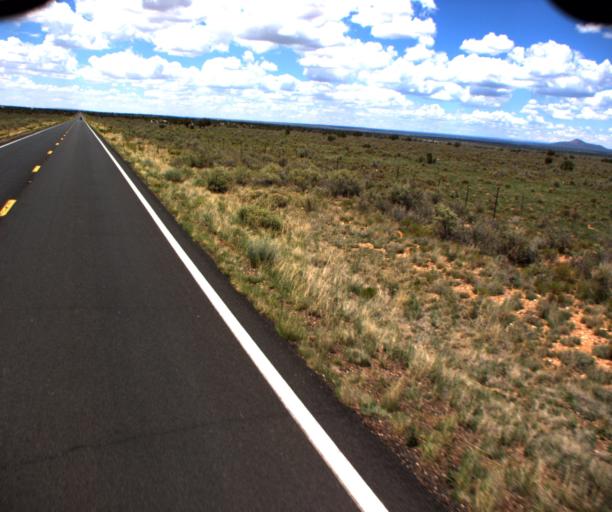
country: US
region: Arizona
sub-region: Coconino County
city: Williams
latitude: 35.6303
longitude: -112.1173
